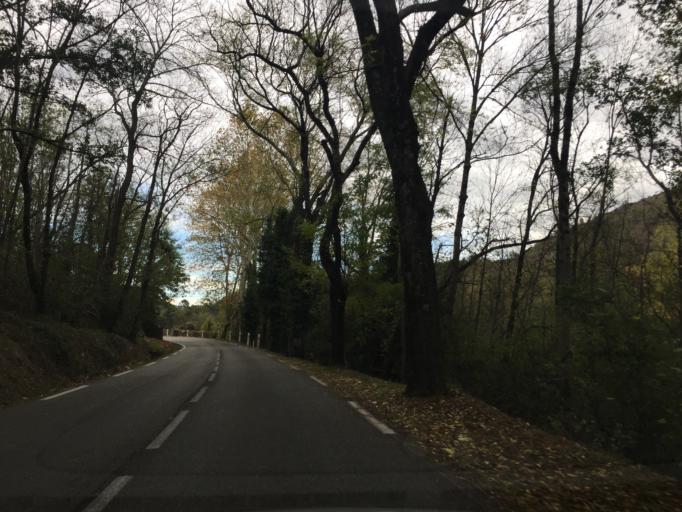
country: FR
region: Rhone-Alpes
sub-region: Departement de l'Ardeche
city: Les Vans
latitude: 44.4156
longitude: 4.1584
